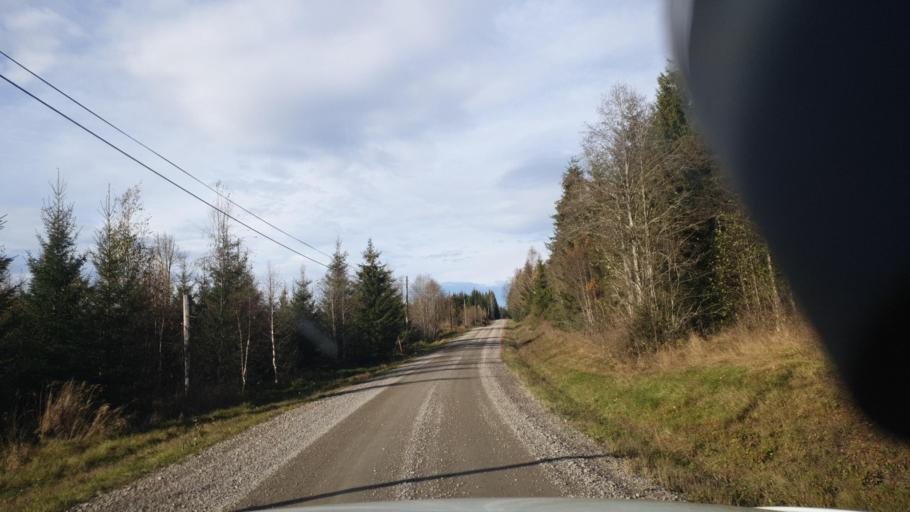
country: SE
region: Vaermland
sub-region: Eda Kommun
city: Charlottenberg
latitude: 59.9726
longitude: 12.4966
